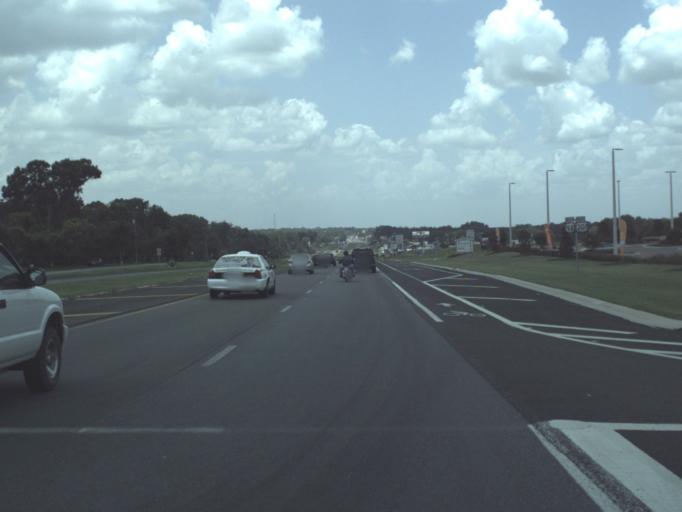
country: US
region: Florida
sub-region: Pasco County
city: Dade City
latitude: 28.3285
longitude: -82.1874
